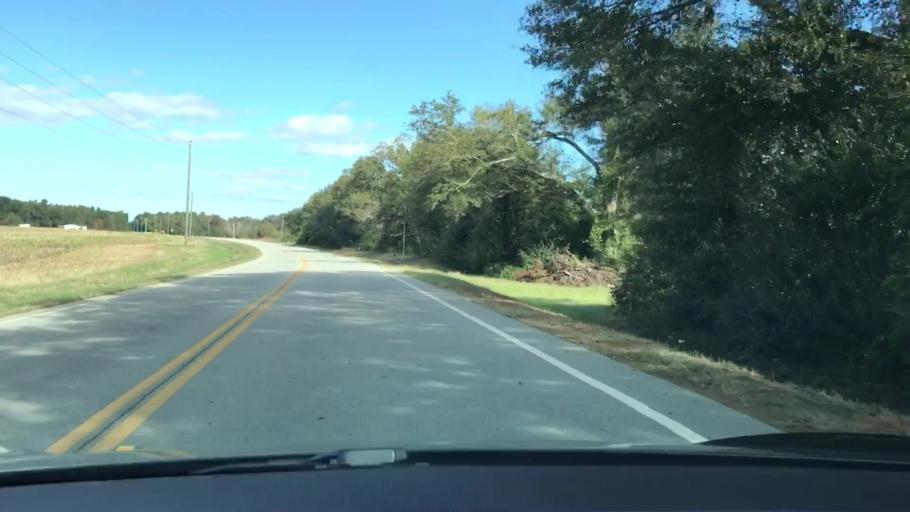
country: US
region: Georgia
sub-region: Jefferson County
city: Wrens
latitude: 33.1786
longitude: -82.4533
